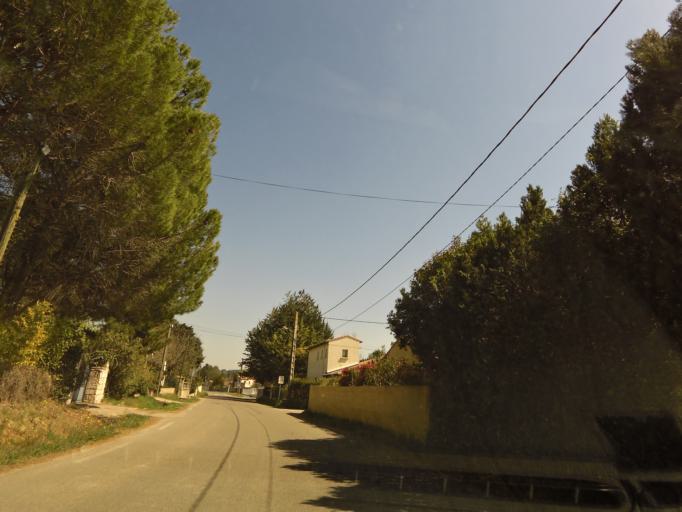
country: FR
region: Languedoc-Roussillon
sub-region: Departement du Gard
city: Calvisson
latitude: 43.7793
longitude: 4.2066
